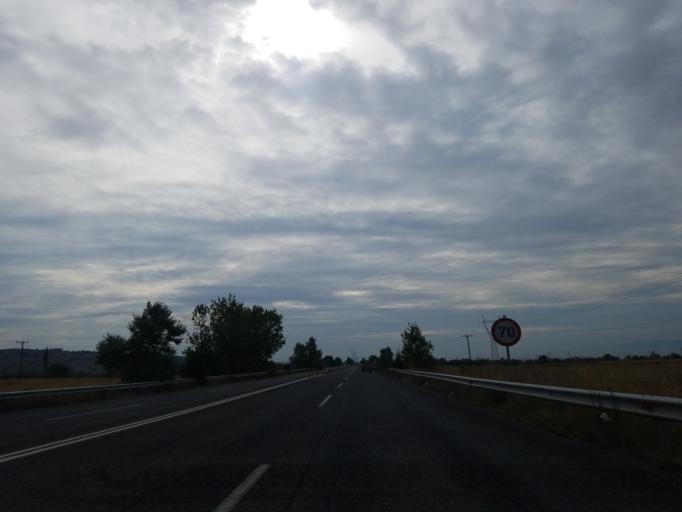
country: GR
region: Thessaly
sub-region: Trikala
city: Vasiliki
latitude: 39.6587
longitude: 21.6765
